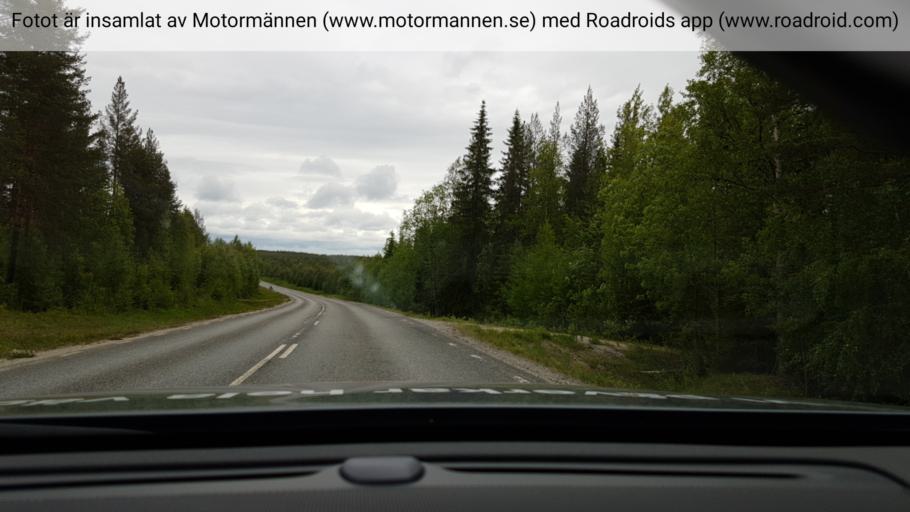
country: SE
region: Vaesterbotten
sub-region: Lycksele Kommun
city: Lycksele
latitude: 64.5193
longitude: 18.4376
